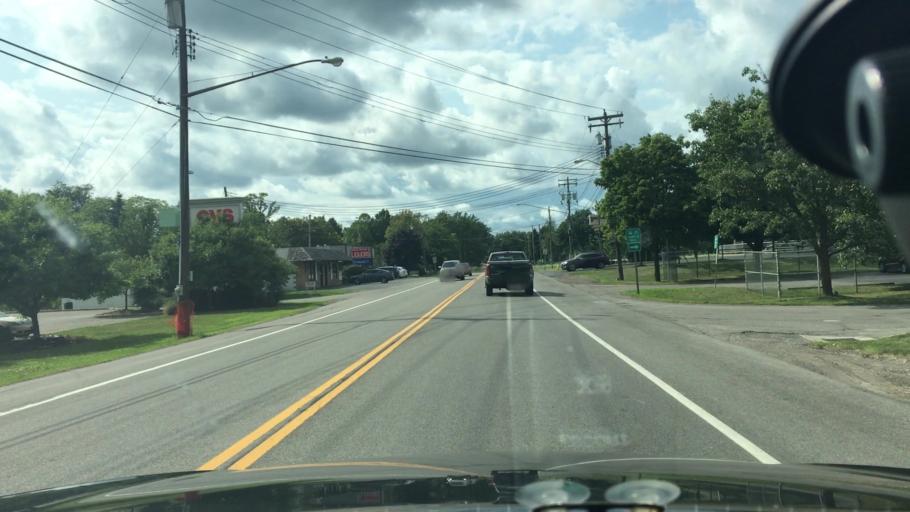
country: US
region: New York
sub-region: Erie County
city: North Boston
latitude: 42.6860
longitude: -78.7770
